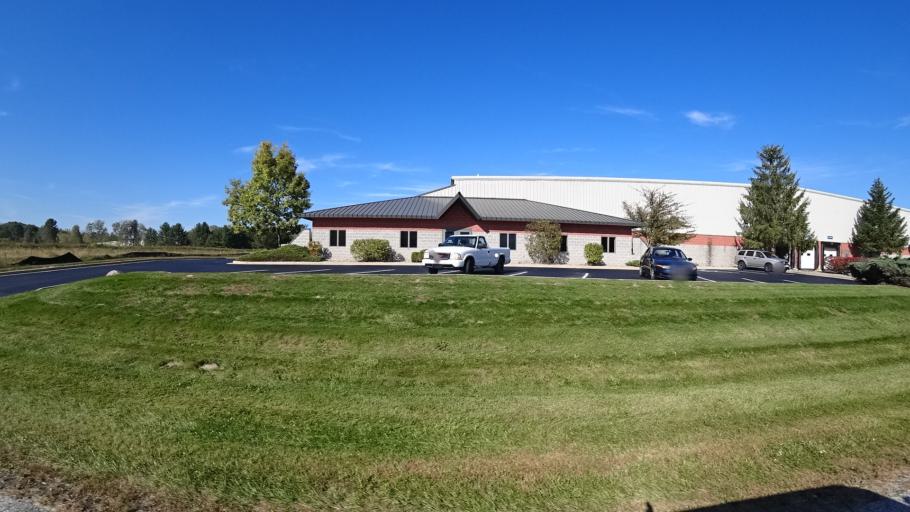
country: US
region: Indiana
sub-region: LaPorte County
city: Trail Creek
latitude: 41.6965
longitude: -86.8401
